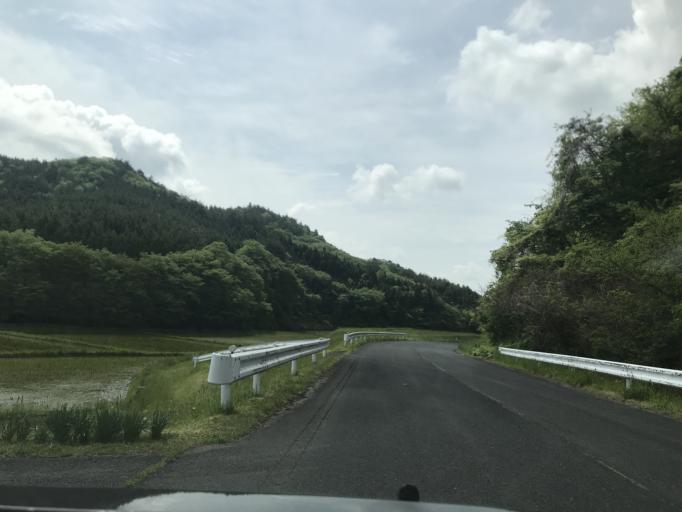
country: JP
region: Iwate
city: Ichinoseki
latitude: 38.8826
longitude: 140.9745
